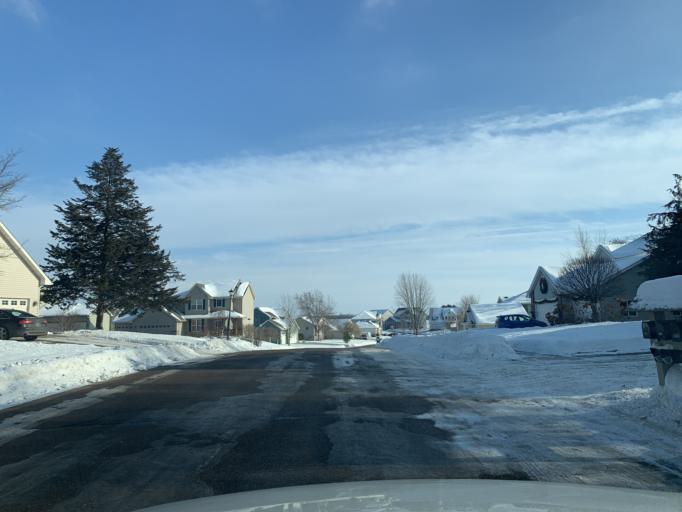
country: US
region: Minnesota
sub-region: Wright County
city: Buffalo
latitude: 45.2040
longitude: -93.8335
